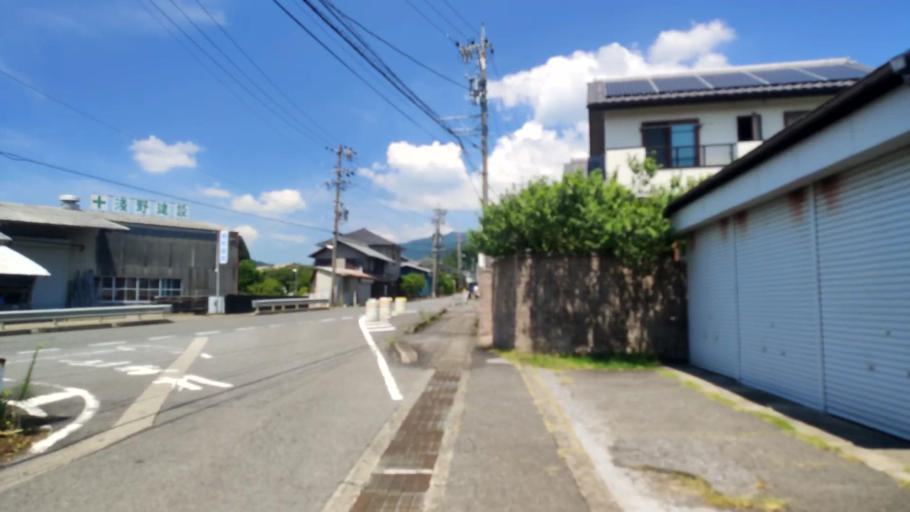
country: JP
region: Gifu
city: Tarui
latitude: 35.3661
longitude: 136.4643
